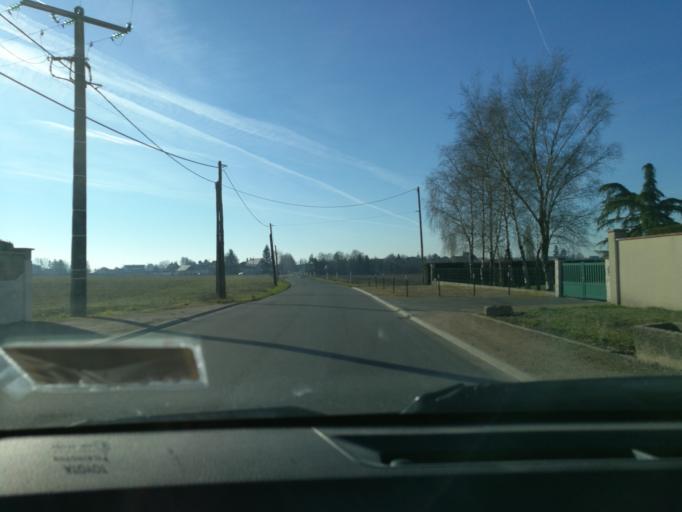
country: FR
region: Centre
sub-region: Departement du Loiret
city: Ingre
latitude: 47.9114
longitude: 1.8033
